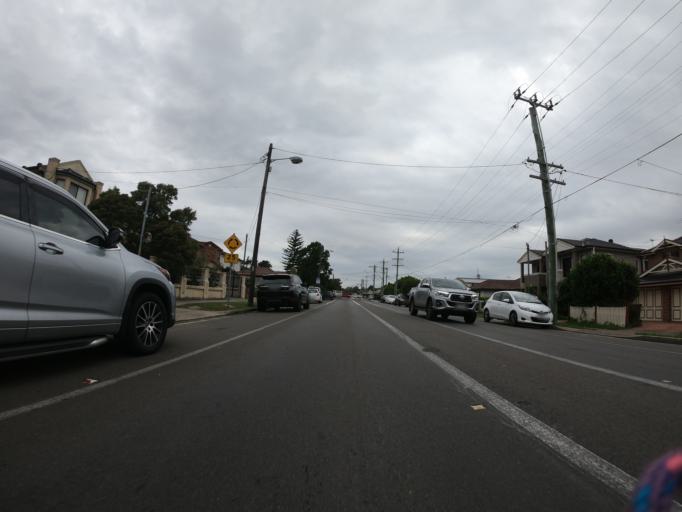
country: AU
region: New South Wales
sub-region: Parramatta
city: Granville
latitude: -33.8434
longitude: 151.0101
